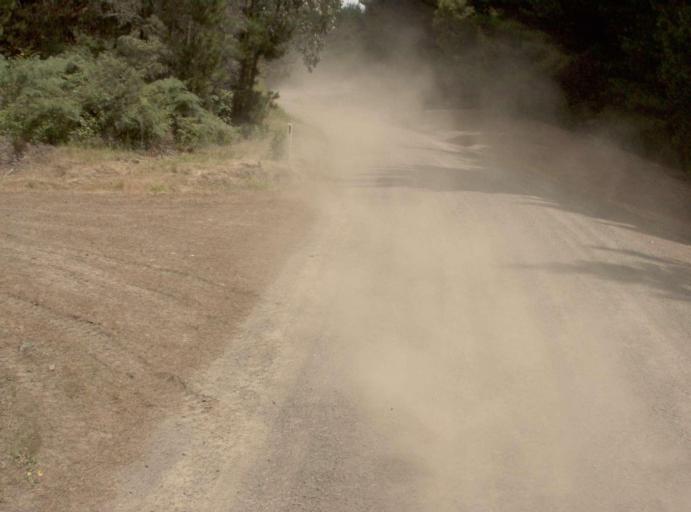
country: AU
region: Victoria
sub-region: Latrobe
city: Traralgon
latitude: -38.3829
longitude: 146.6654
